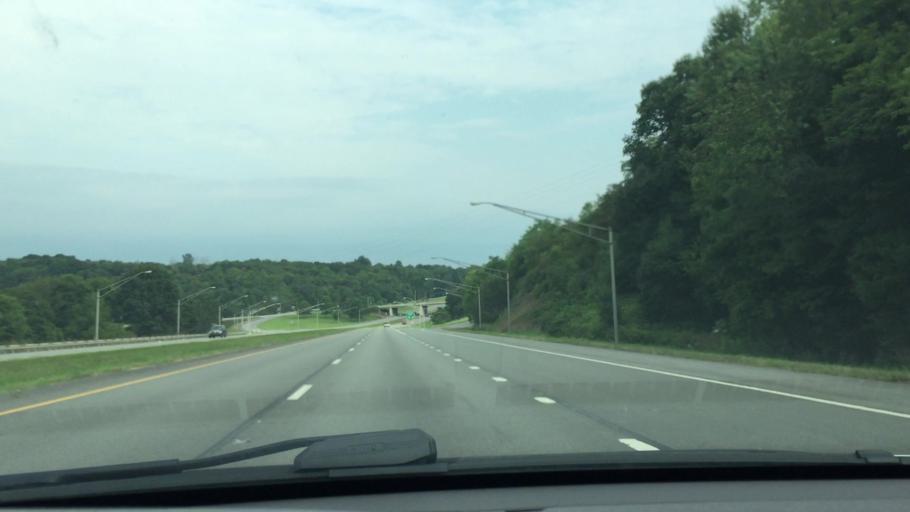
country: US
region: Pennsylvania
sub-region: Beaver County
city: New Brighton
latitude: 40.7052
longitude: -80.3701
